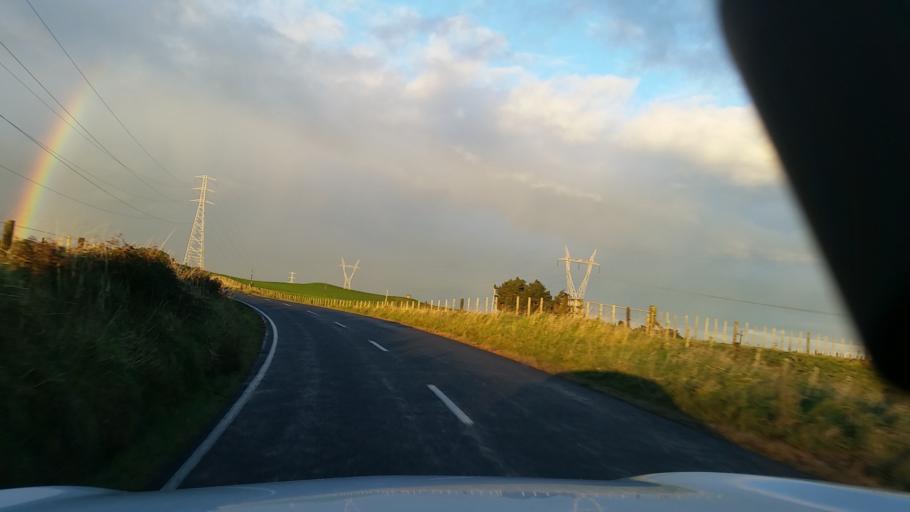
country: NZ
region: Manawatu-Wanganui
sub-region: Wanganui District
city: Wanganui
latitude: -39.8010
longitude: 174.8206
